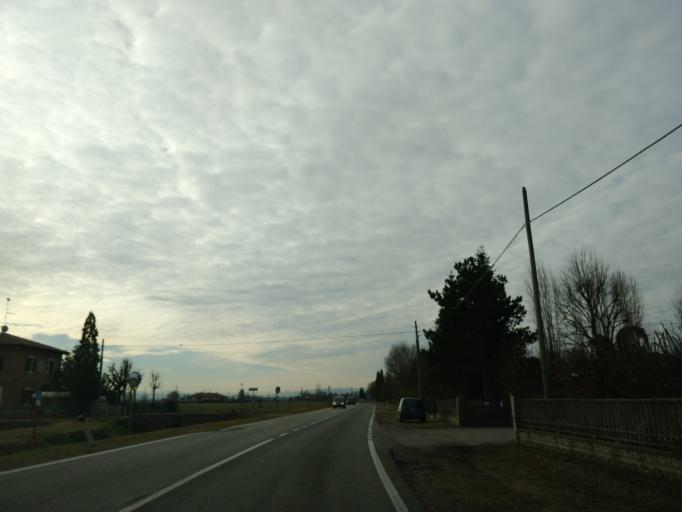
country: IT
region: Emilia-Romagna
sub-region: Provincia di Bologna
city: Argelato
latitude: 44.6327
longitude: 11.3437
